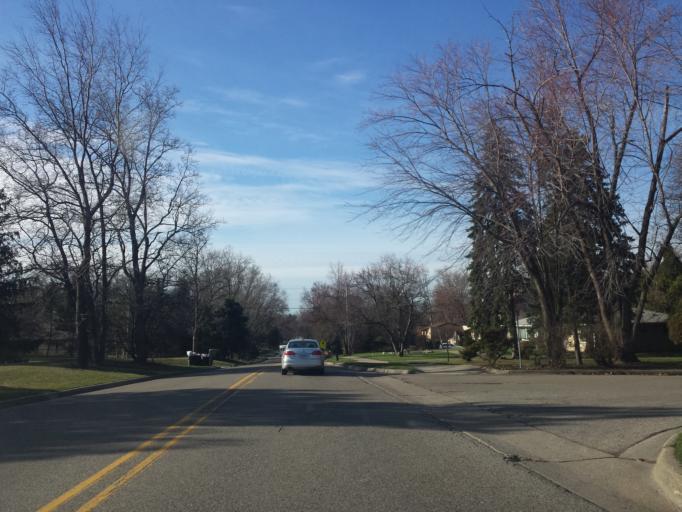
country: US
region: Michigan
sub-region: Oakland County
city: Bloomfield Hills
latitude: 42.6031
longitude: -83.2663
